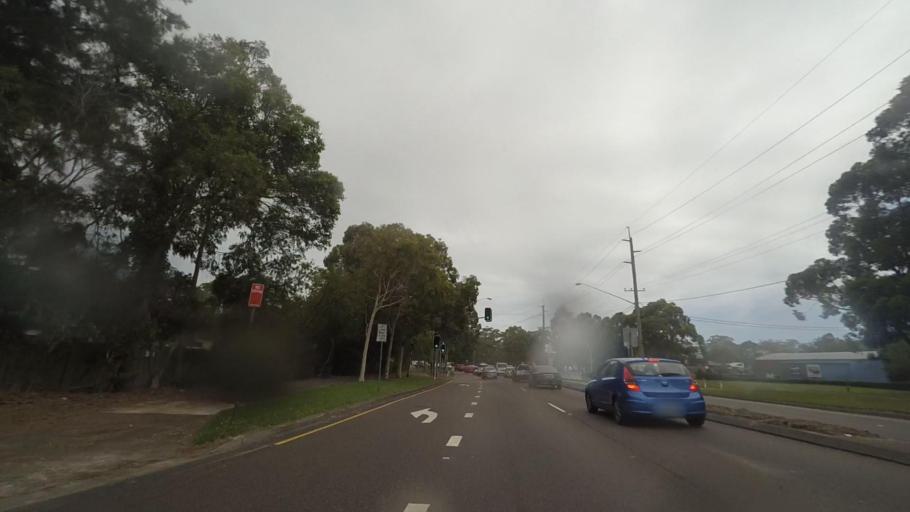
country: AU
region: New South Wales
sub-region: Wyong Shire
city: Tumbi Vmbi
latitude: -33.3612
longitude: 151.4433
